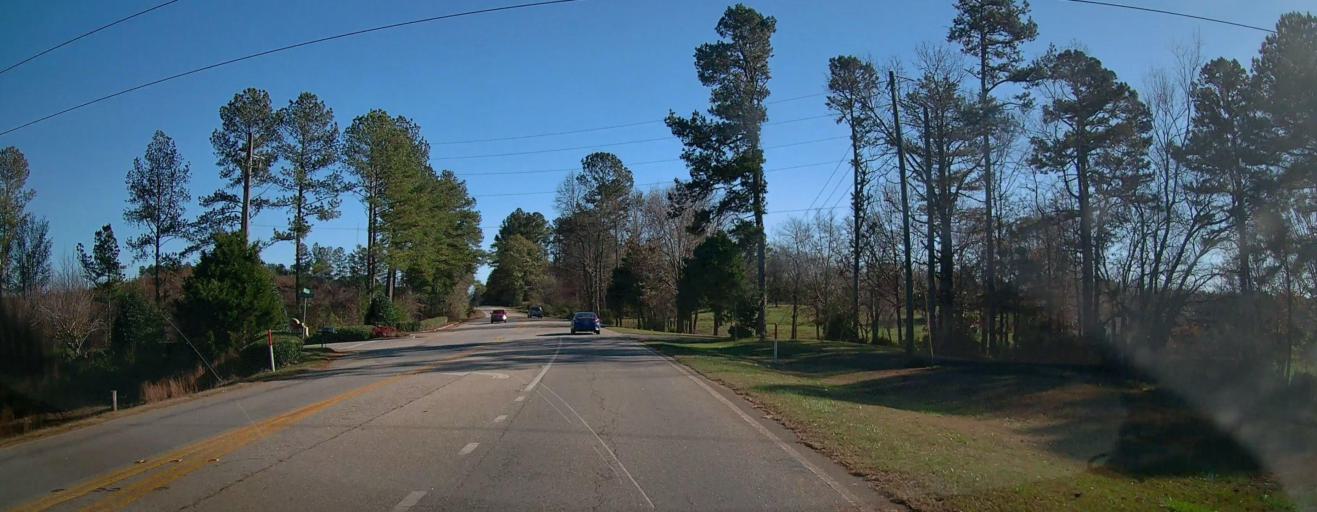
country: US
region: Georgia
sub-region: Hall County
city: Lula
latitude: 34.4015
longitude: -83.6976
